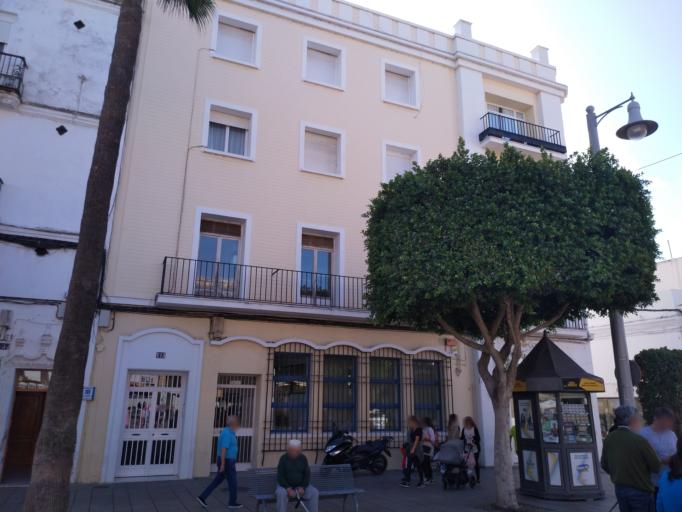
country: ES
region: Andalusia
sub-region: Provincia de Cadiz
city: San Fernando
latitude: 36.4644
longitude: -6.1980
